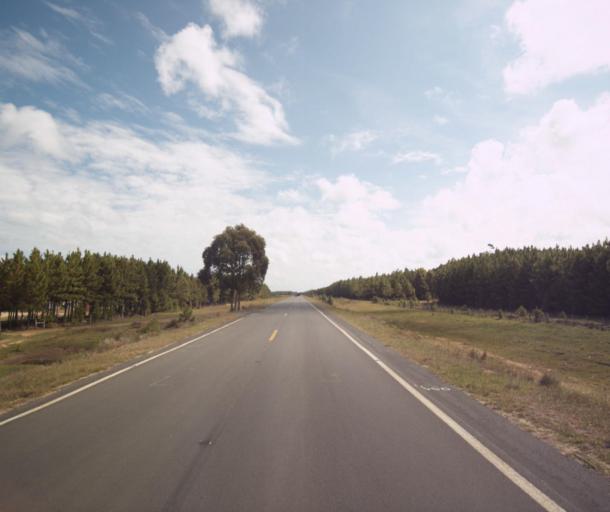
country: BR
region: Rio Grande do Sul
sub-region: Sao Lourenco Do Sul
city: Sao Lourenco do Sul
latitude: -31.4489
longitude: -51.2101
